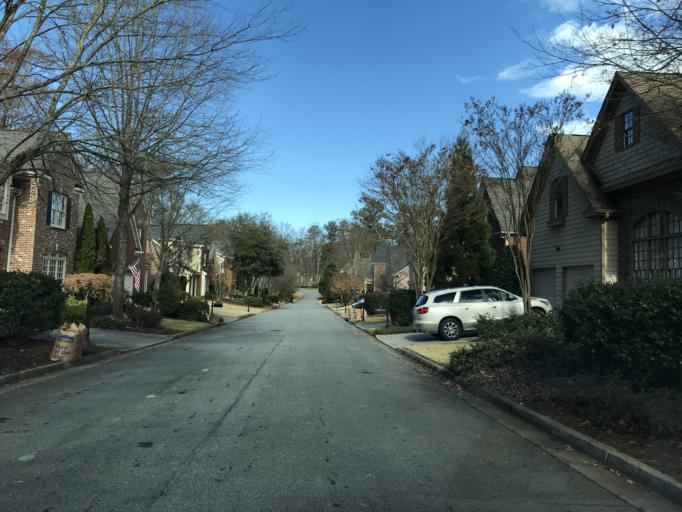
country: US
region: Georgia
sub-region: DeKalb County
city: North Atlanta
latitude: 33.8841
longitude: -84.3478
